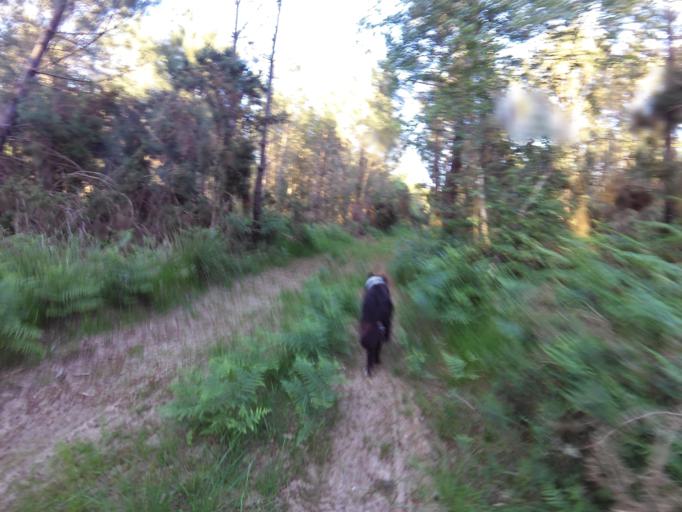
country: FR
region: Brittany
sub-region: Departement du Morbihan
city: Molac
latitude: 47.7454
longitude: -2.4164
